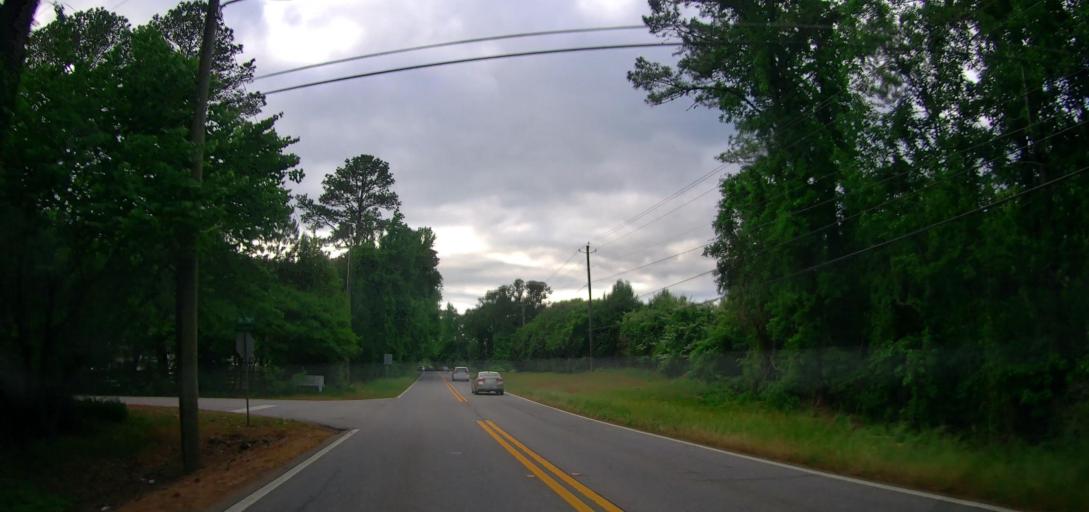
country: US
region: Georgia
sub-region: Clarke County
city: Athens
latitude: 33.9299
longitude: -83.4152
